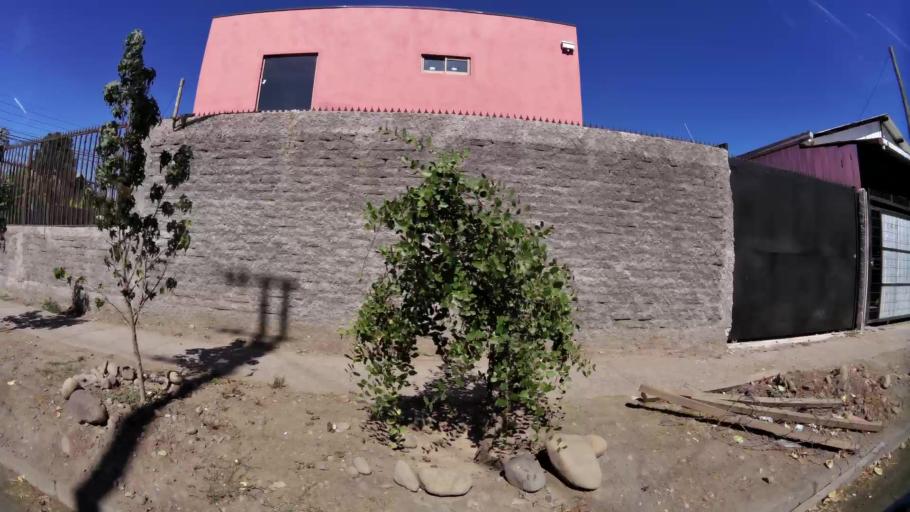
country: CL
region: O'Higgins
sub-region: Provincia de Colchagua
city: Chimbarongo
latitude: -34.5890
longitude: -70.9995
